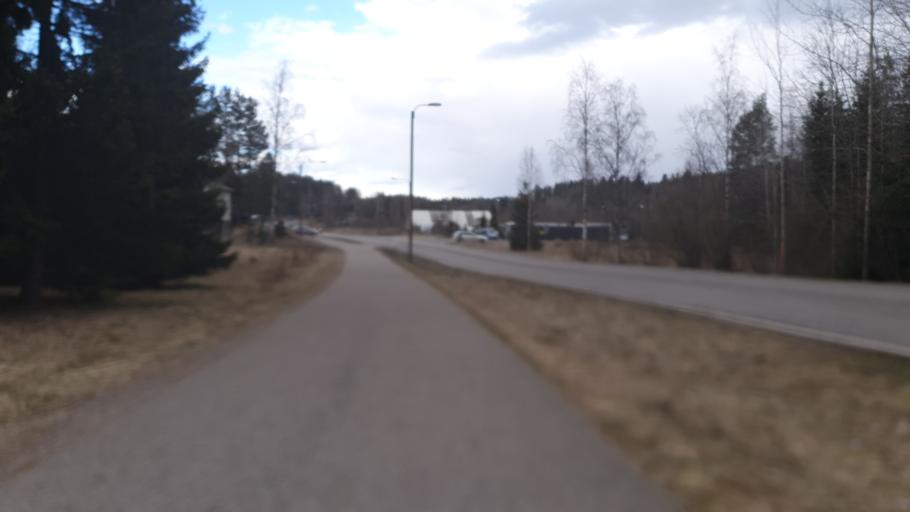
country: FI
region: Uusimaa
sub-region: Helsinki
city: Nurmijaervi
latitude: 60.3655
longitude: 24.7505
